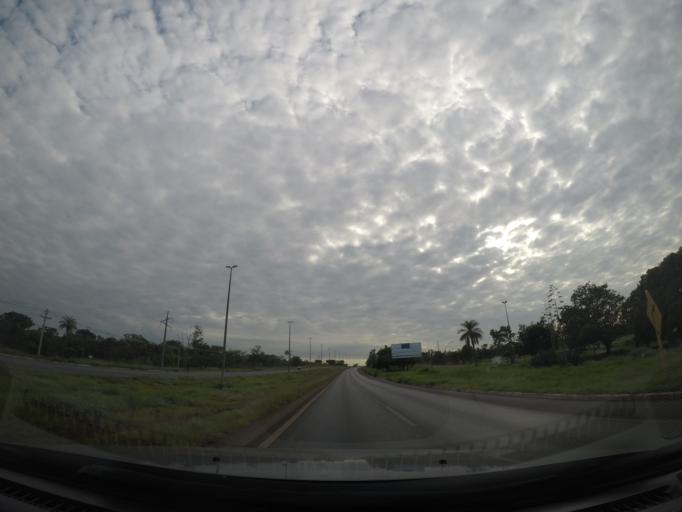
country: BR
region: Goias
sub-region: Planaltina
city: Planaltina
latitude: -15.5953
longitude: -47.6678
